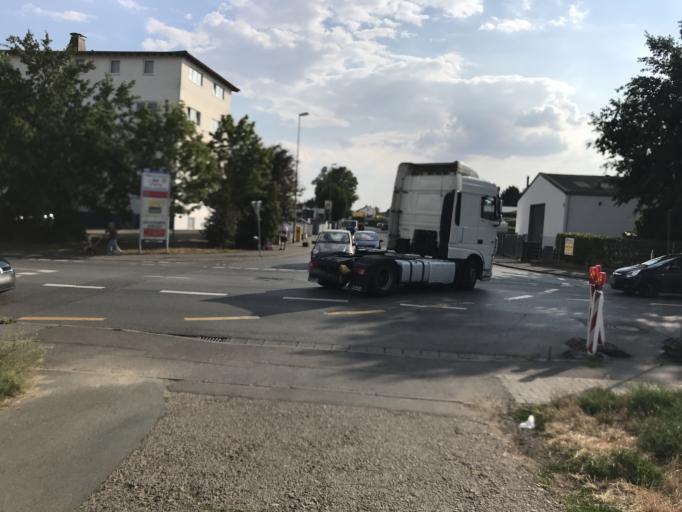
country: DE
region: Rheinland-Pfalz
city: Mainz
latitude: 50.0179
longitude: 8.2918
